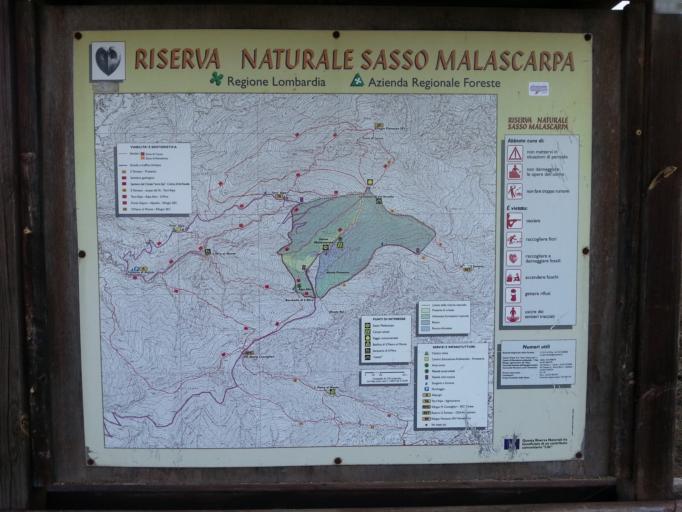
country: IT
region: Lombardy
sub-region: Provincia di Lecco
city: Suello
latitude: 45.8488
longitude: 9.3167
